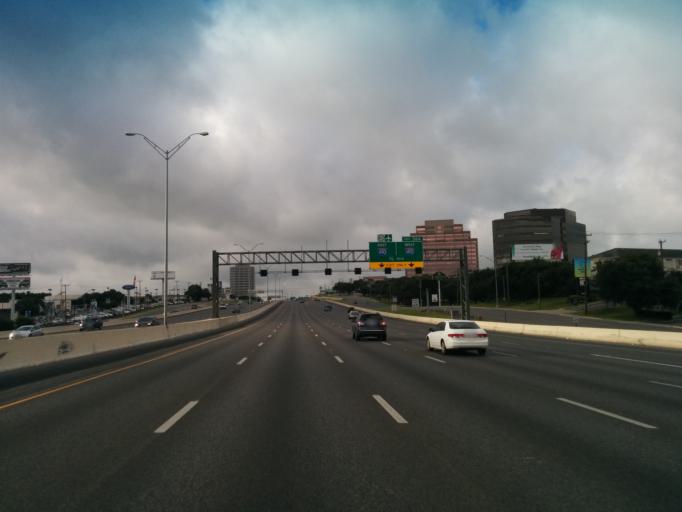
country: US
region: Texas
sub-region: Bexar County
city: Balcones Heights
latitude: 29.5194
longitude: -98.5548
